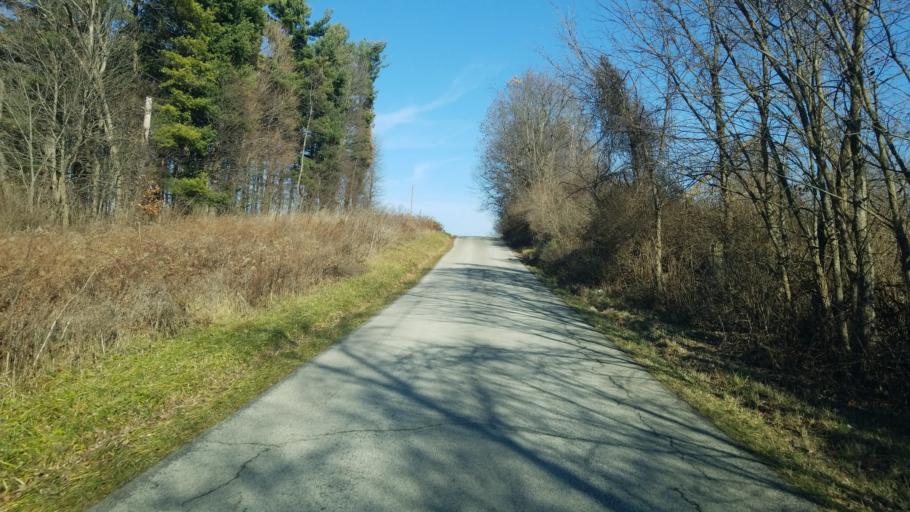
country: US
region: Ohio
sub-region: Licking County
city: Utica
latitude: 40.1760
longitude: -82.4505
